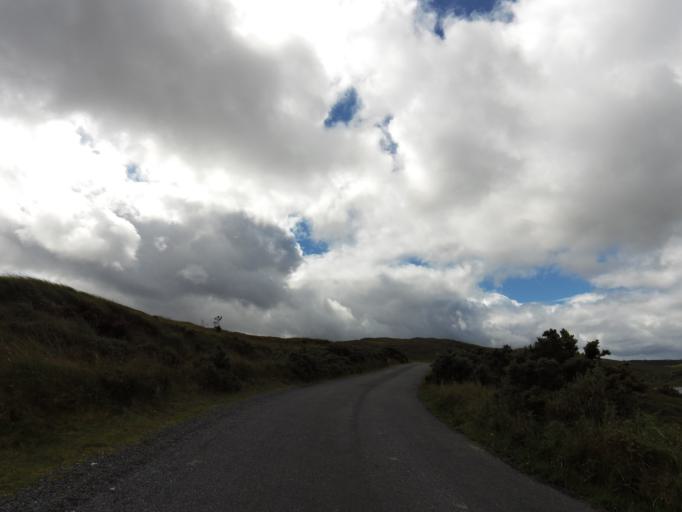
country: IE
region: Connaught
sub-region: County Galway
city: Oughterard
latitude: 53.3980
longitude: -9.3321
